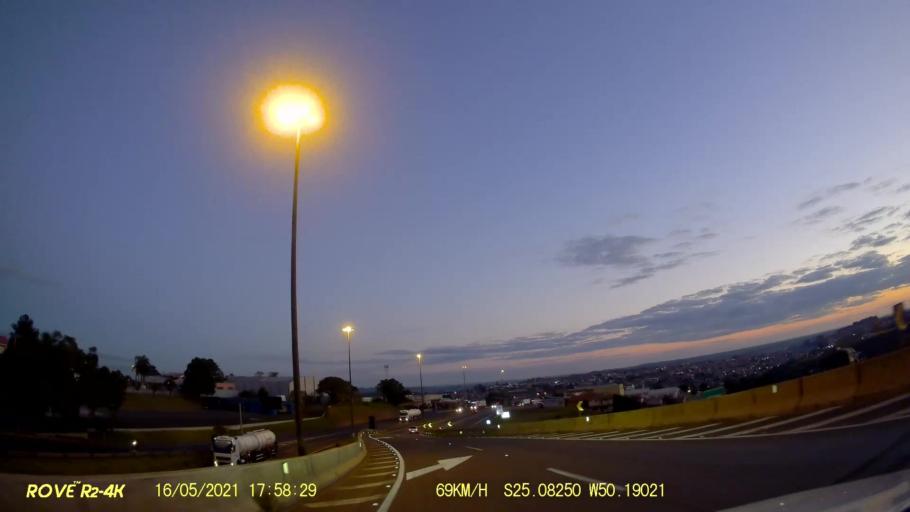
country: BR
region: Parana
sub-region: Ponta Grossa
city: Ponta Grossa
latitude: -25.0822
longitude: -50.1899
